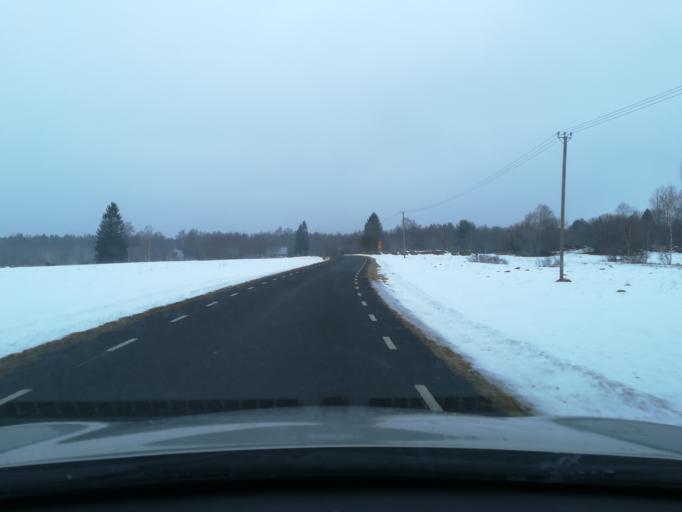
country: EE
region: Harju
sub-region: Loksa linn
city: Loksa
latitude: 59.4706
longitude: 25.6931
